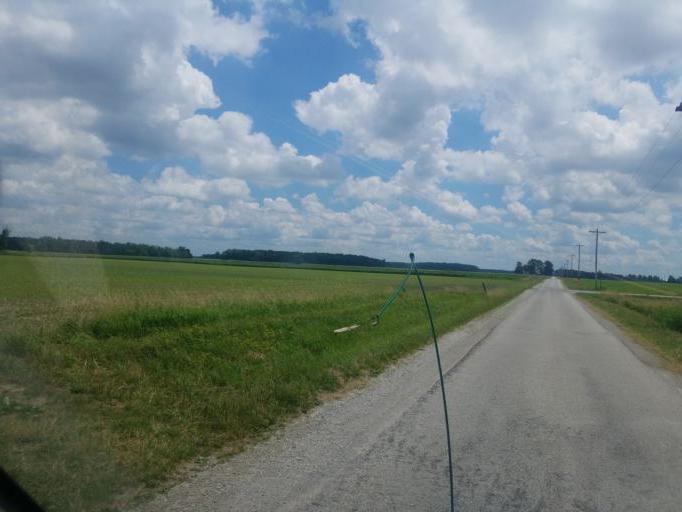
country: US
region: Ohio
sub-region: Huron County
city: Willard
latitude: 41.0305
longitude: -82.8307
